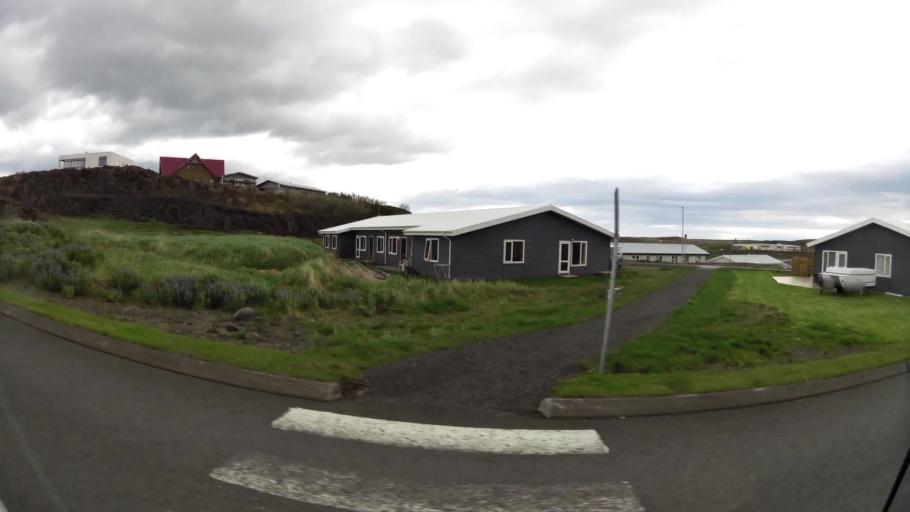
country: IS
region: West
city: Borgarnes
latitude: 64.5563
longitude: -21.8958
